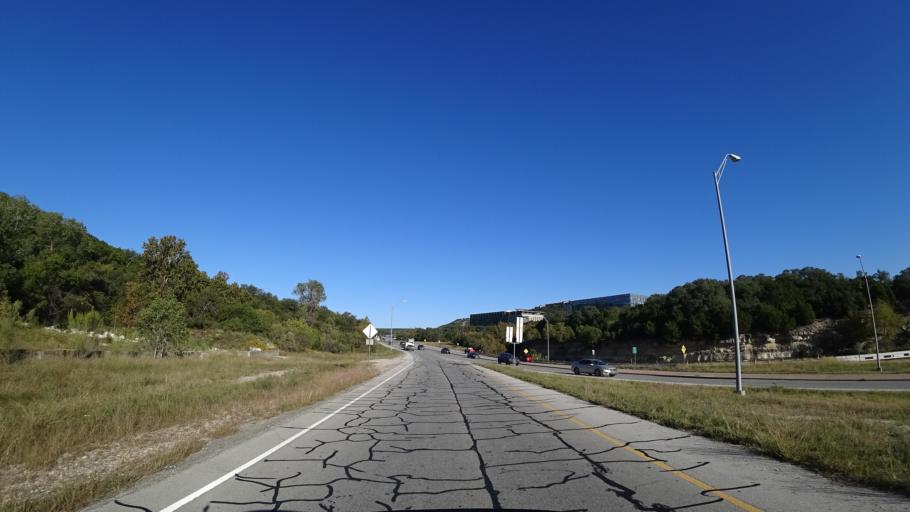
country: US
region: Texas
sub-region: Travis County
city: West Lake Hills
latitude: 30.3594
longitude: -97.7927
